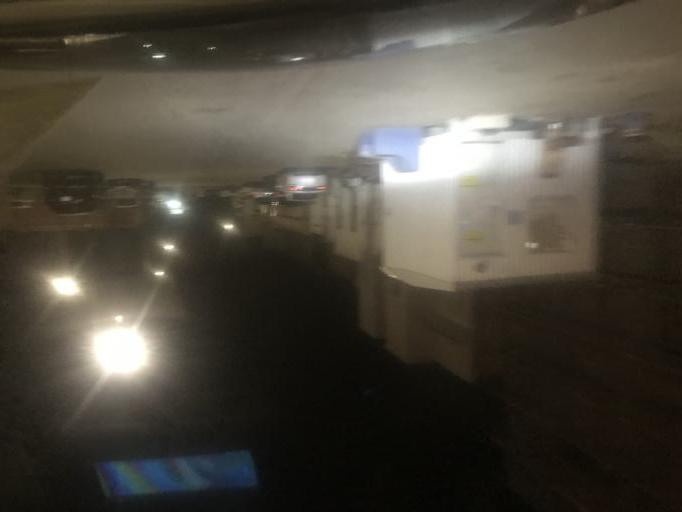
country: SA
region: Ar Riyad
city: Riyadh
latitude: 24.6914
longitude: 46.5984
